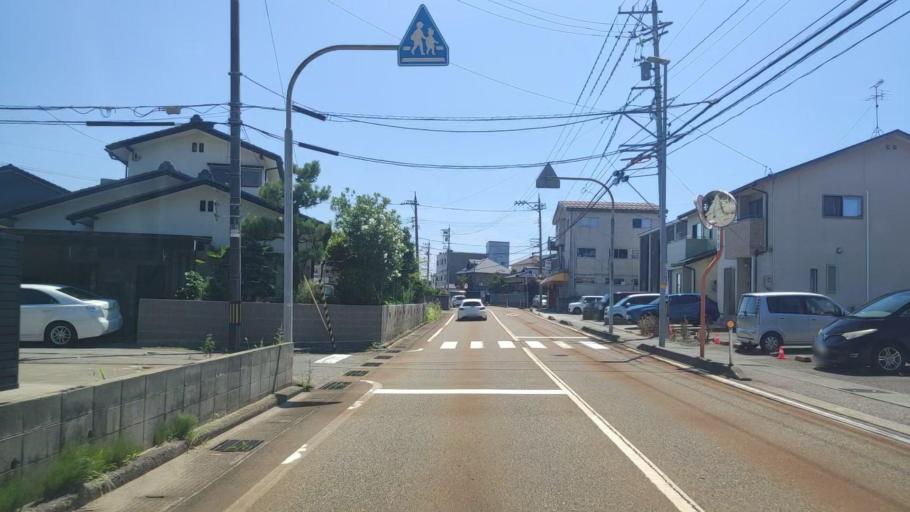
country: JP
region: Ishikawa
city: Kanazawa-shi
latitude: 36.6419
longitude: 136.6425
